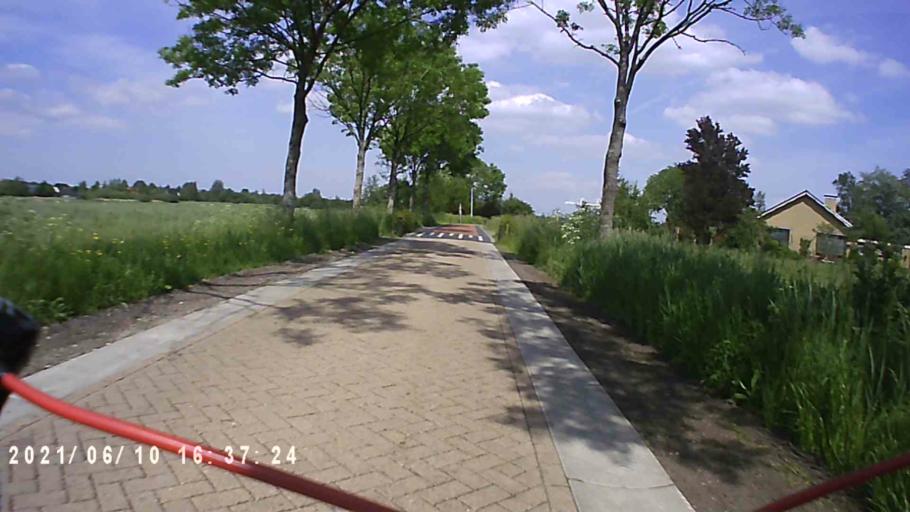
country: NL
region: Friesland
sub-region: Gemeente Achtkarspelen
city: Buitenpost
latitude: 53.2401
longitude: 6.1429
